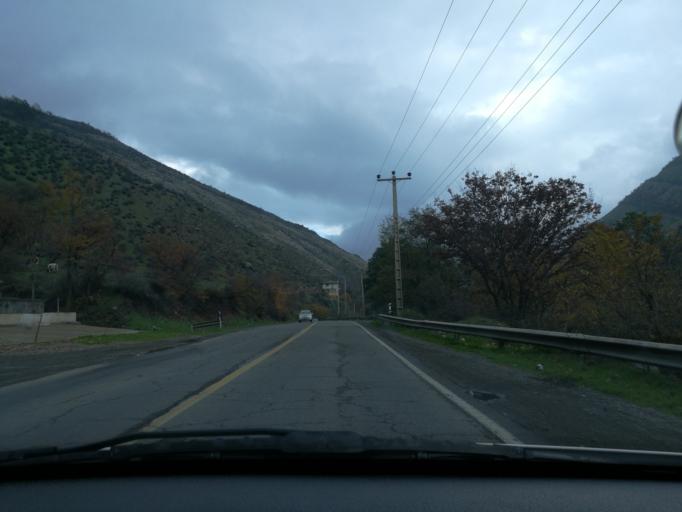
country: IR
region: Mazandaran
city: Chalus
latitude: 36.3672
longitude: 51.2632
